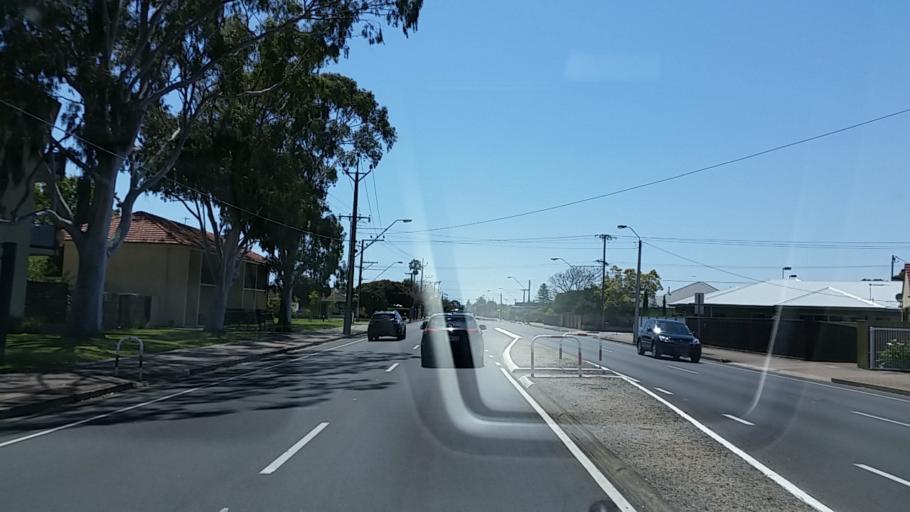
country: AU
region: South Australia
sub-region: Holdfast Bay
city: North Brighton
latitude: -34.9937
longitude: 138.5283
